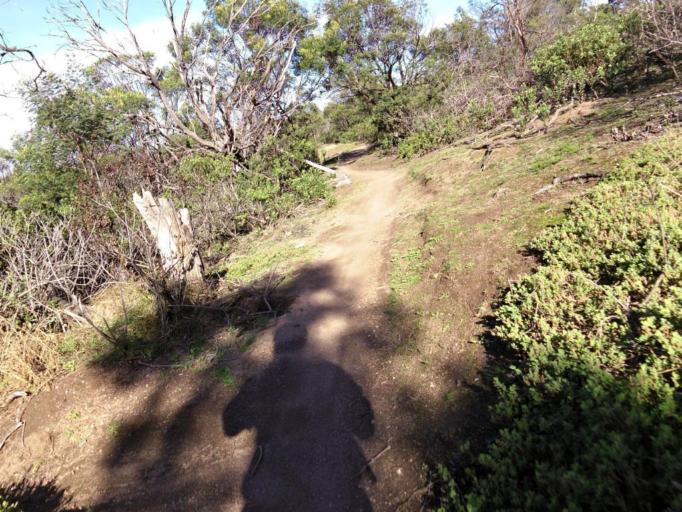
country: AU
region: Victoria
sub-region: Wyndham
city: Little River
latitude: -37.9281
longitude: 144.4308
